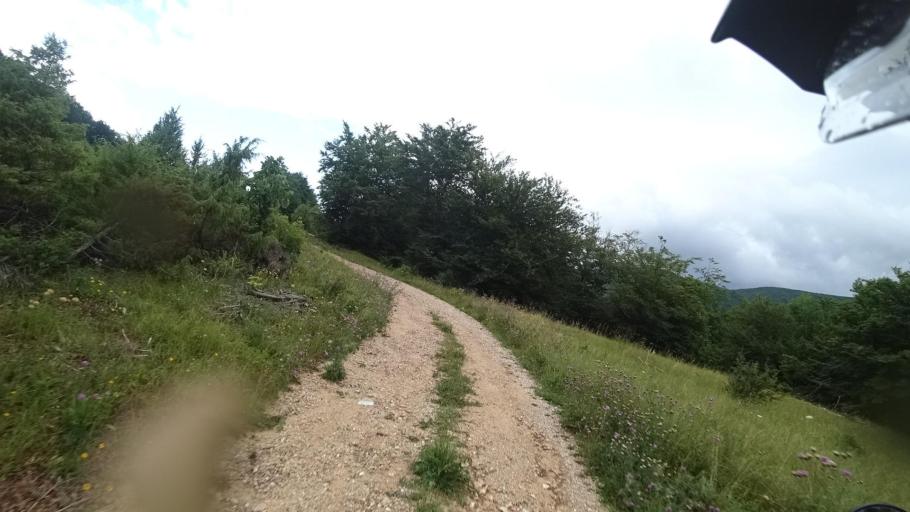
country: HR
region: Licko-Senjska
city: Jezerce
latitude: 44.7327
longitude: 15.6364
